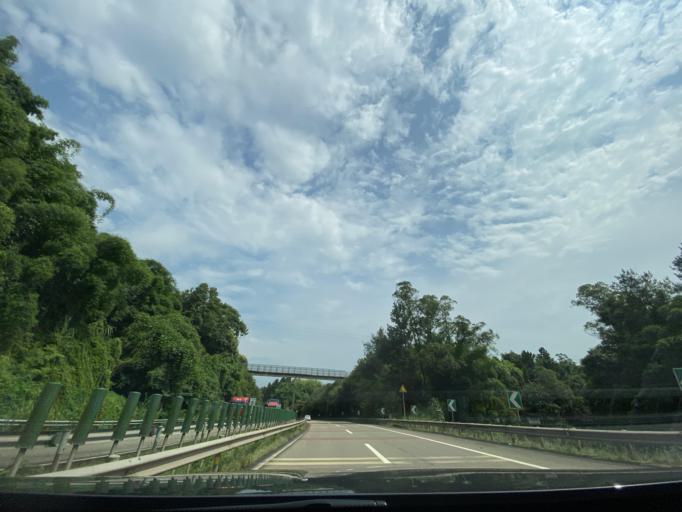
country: CN
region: Sichuan
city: Chonglong
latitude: 29.8021
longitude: 104.7101
